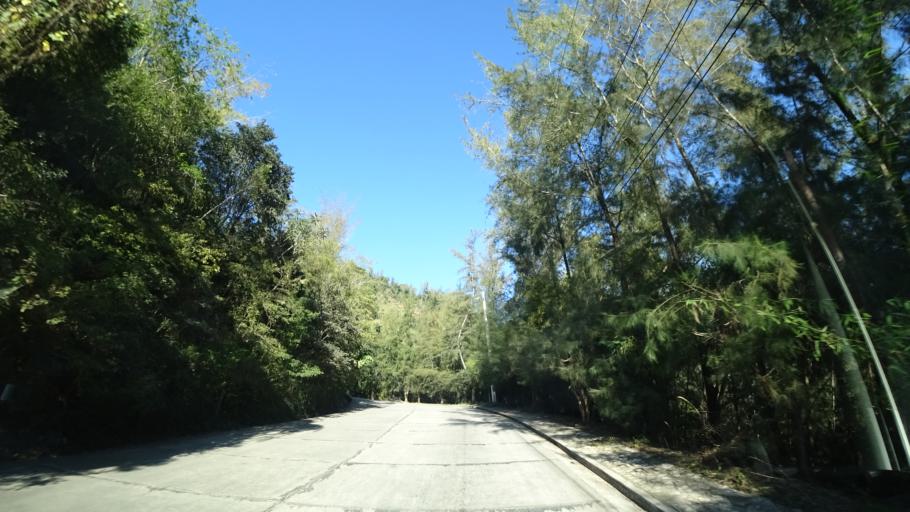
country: HT
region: Ouest
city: Port-au-Prince
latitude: 18.4961
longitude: -72.3490
